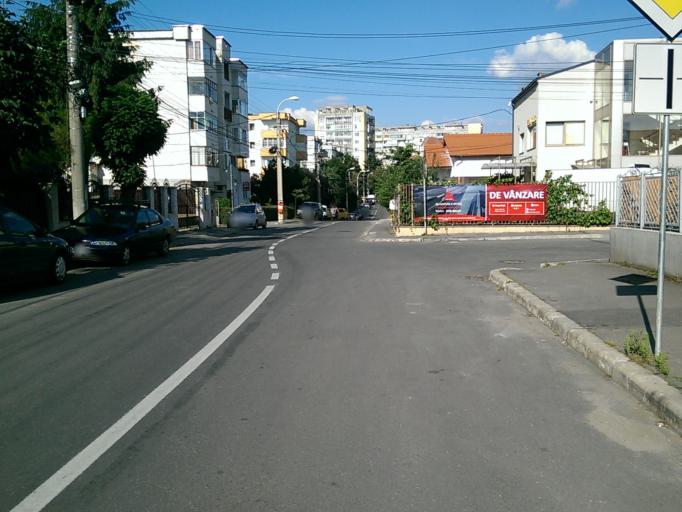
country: RO
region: Cluj
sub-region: Municipiul Cluj-Napoca
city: Cluj-Napoca
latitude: 46.7666
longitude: 23.6165
